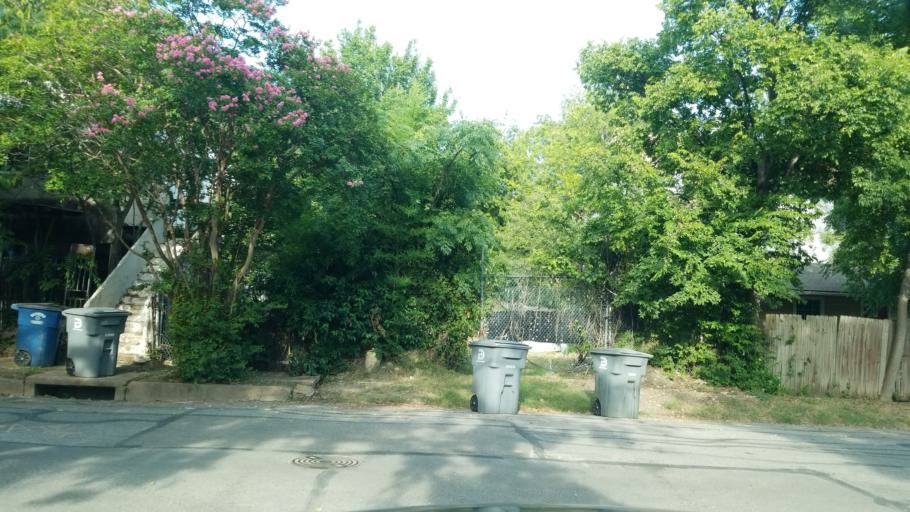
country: US
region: Texas
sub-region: Dallas County
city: Highland Park
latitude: 32.8127
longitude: -96.7670
